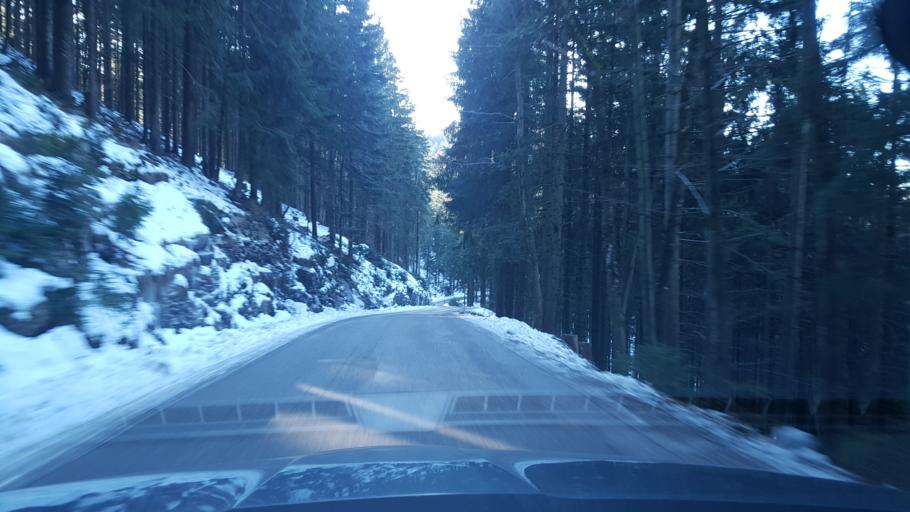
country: AT
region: Salzburg
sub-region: Politischer Bezirk Hallein
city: Scheffau am Tennengebirge
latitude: 47.6361
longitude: 13.2363
